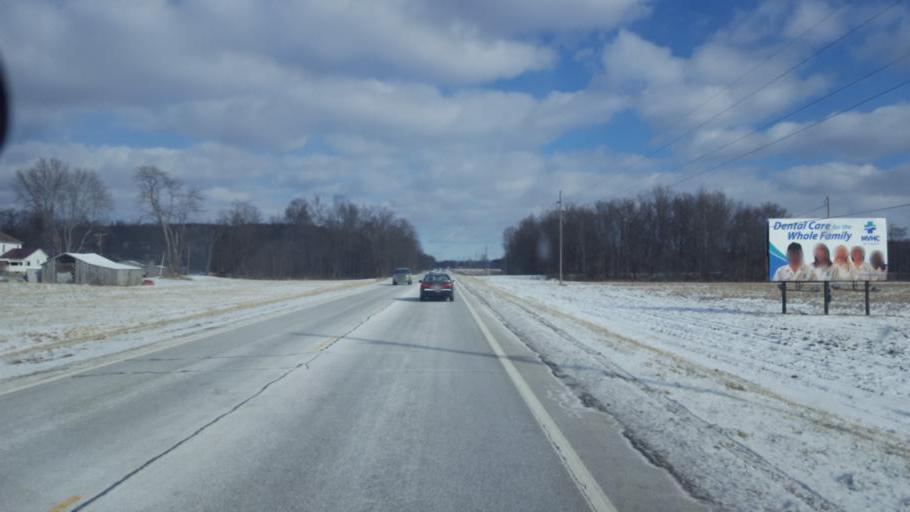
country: US
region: Ohio
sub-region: Coshocton County
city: Coshocton
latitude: 40.1984
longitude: -81.8914
